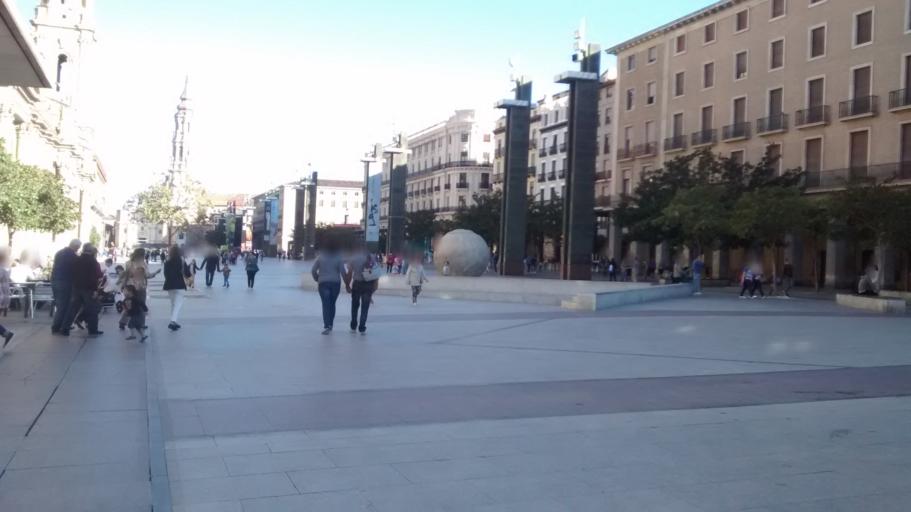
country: ES
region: Aragon
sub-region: Provincia de Zaragoza
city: Zaragoza
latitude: 41.6569
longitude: -0.8802
